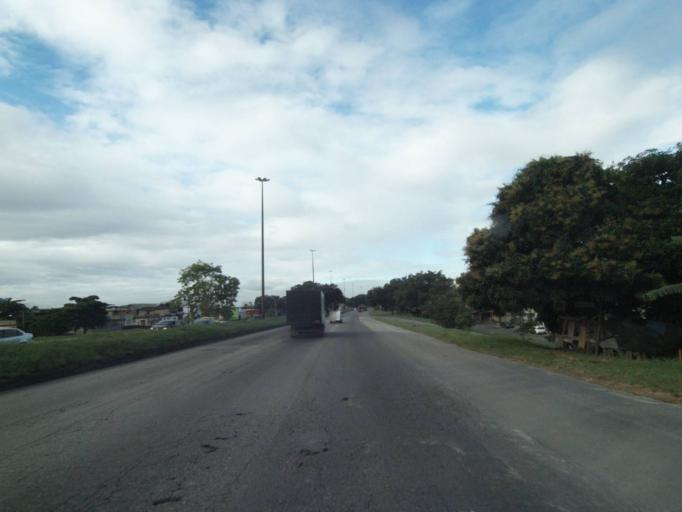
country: BR
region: Rio de Janeiro
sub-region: Nilopolis
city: Nilopolis
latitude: -22.8556
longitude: -43.4919
